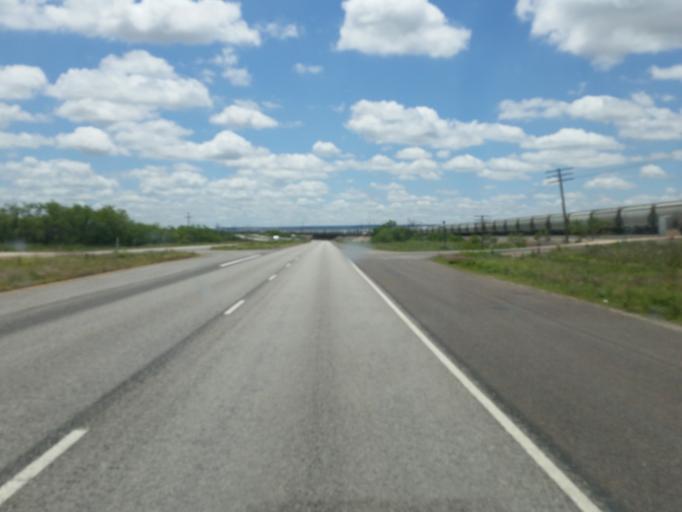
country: US
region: Texas
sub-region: Garza County
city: Post
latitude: 33.0432
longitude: -101.2033
